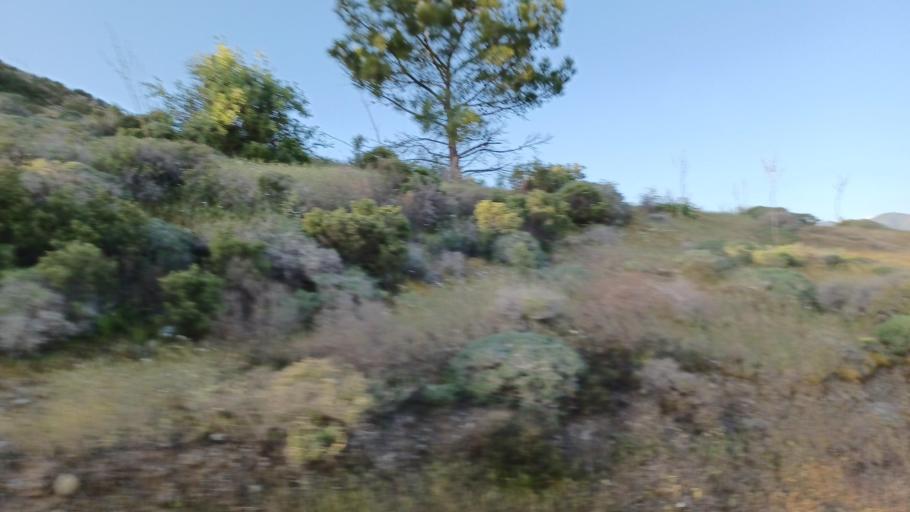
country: CY
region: Lefkosia
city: Astromeritis
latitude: 35.0682
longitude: 33.0366
